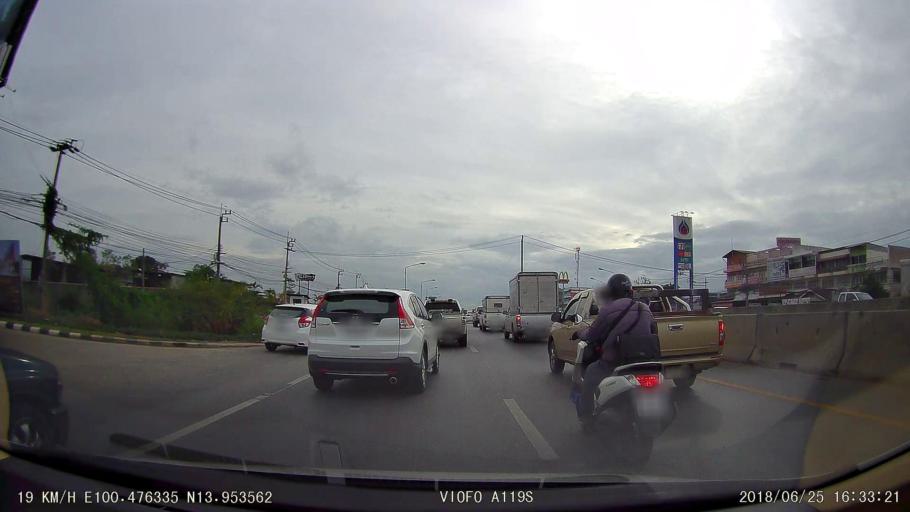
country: TH
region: Nonthaburi
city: Pak Kret
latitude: 13.9535
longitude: 100.4763
